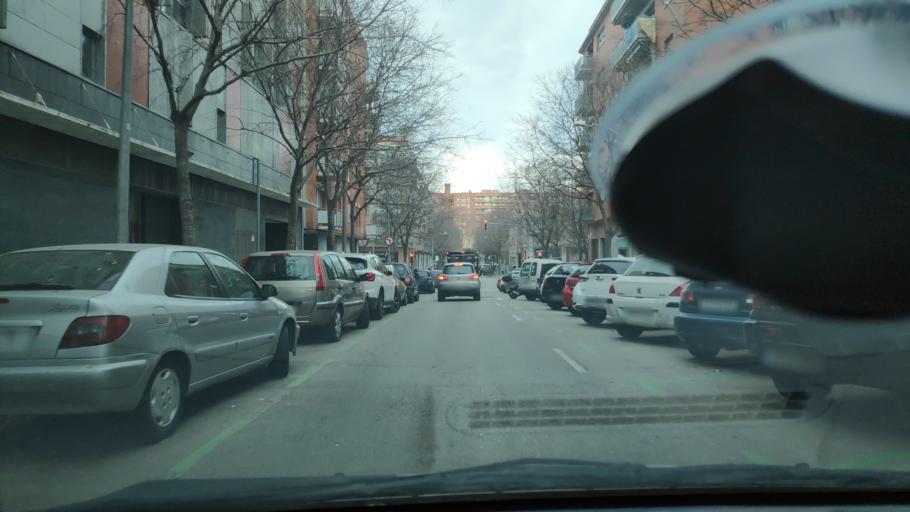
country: ES
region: Catalonia
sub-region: Provincia de Barcelona
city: Sant Marti
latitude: 41.4062
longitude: 2.1968
